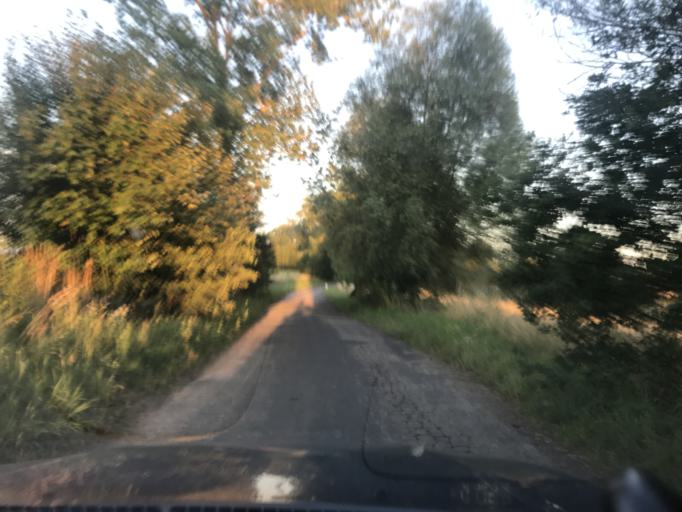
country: PL
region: West Pomeranian Voivodeship
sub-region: Powiat stargardzki
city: Chociwel
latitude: 53.4698
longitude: 15.3679
